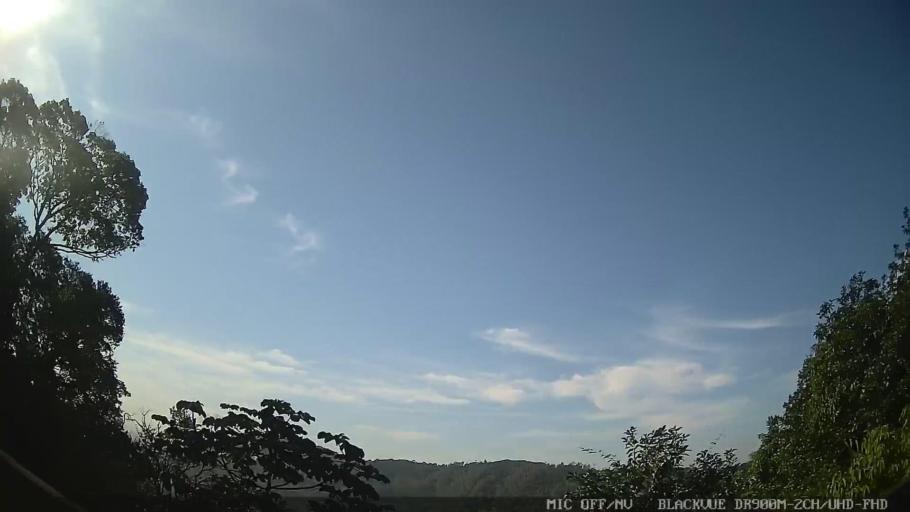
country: BR
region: Sao Paulo
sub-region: Cubatao
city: Cubatao
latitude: -23.8878
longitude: -46.4627
